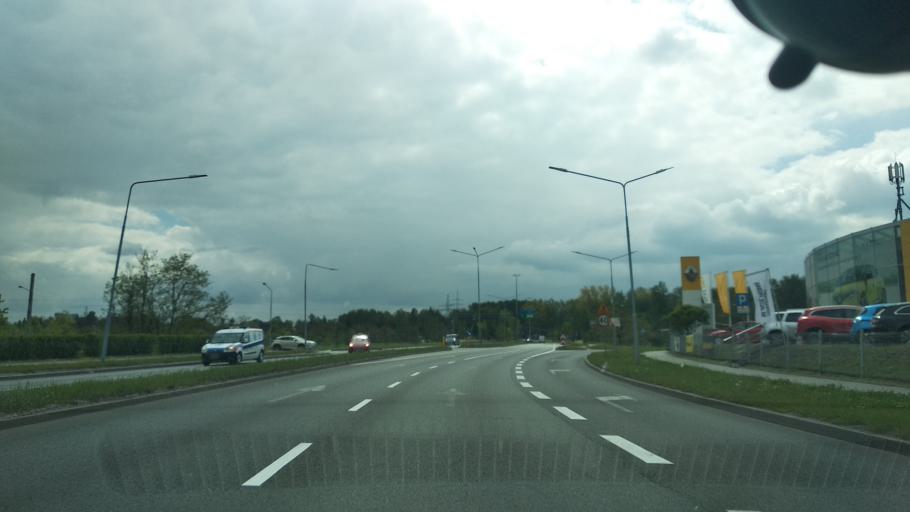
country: PL
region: Silesian Voivodeship
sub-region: Katowice
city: Katowice
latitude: 50.2550
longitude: 18.9839
